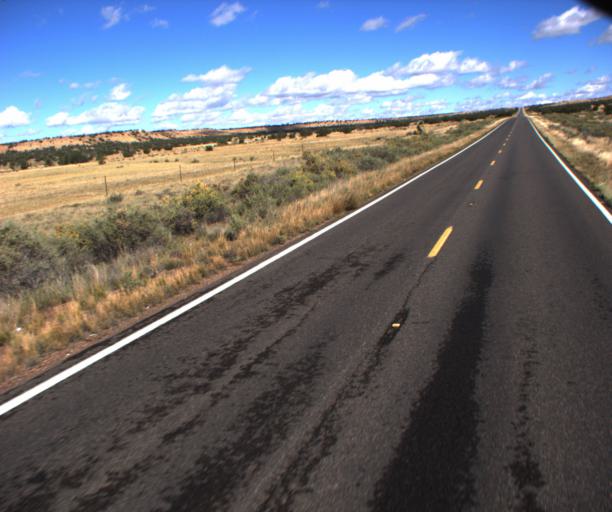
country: US
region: Arizona
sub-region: Apache County
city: Saint Johns
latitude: 34.7976
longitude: -109.2380
